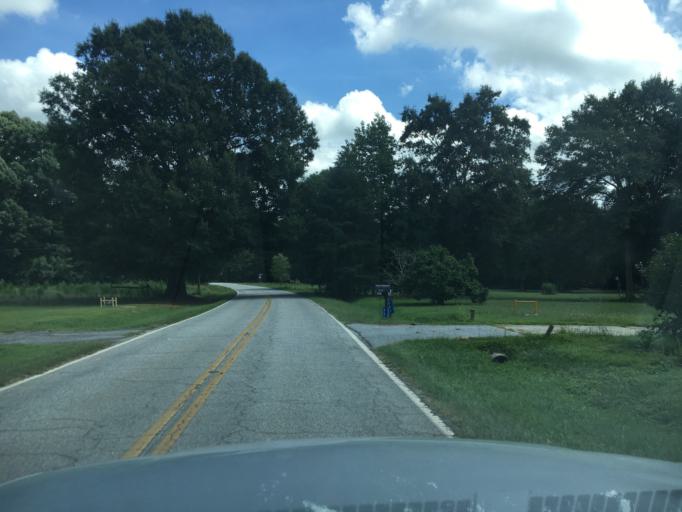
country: US
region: South Carolina
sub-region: Anderson County
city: Belton
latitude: 34.5672
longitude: -82.4839
